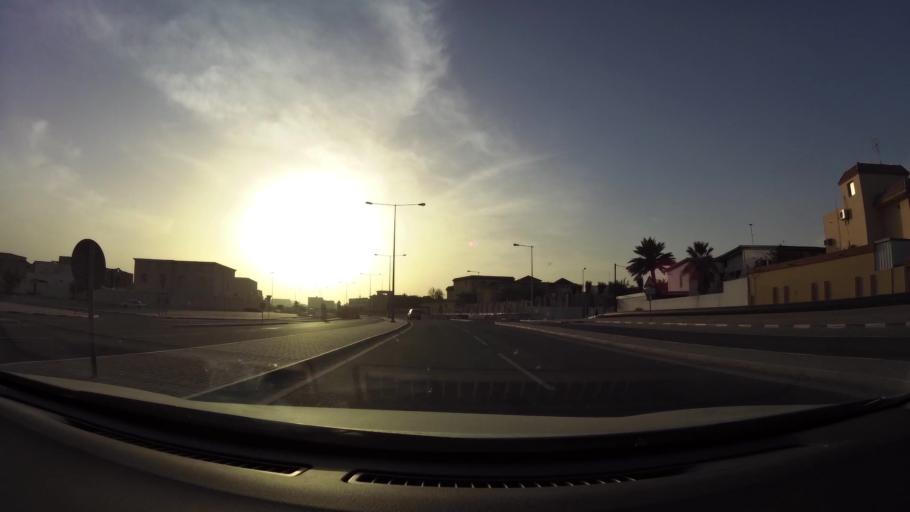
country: QA
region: Al Wakrah
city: Al Wakrah
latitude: 25.1518
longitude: 51.5972
